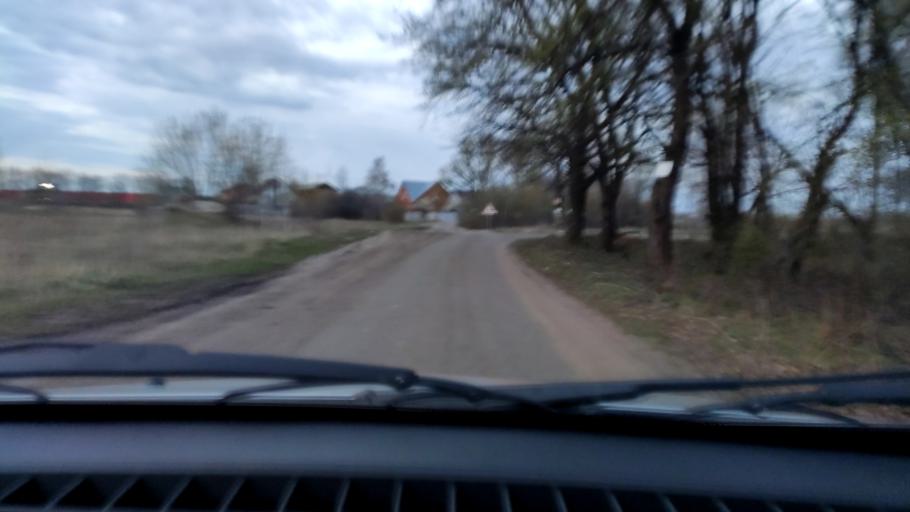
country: RU
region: Voronezj
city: Podgornoye
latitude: 51.7941
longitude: 39.2139
